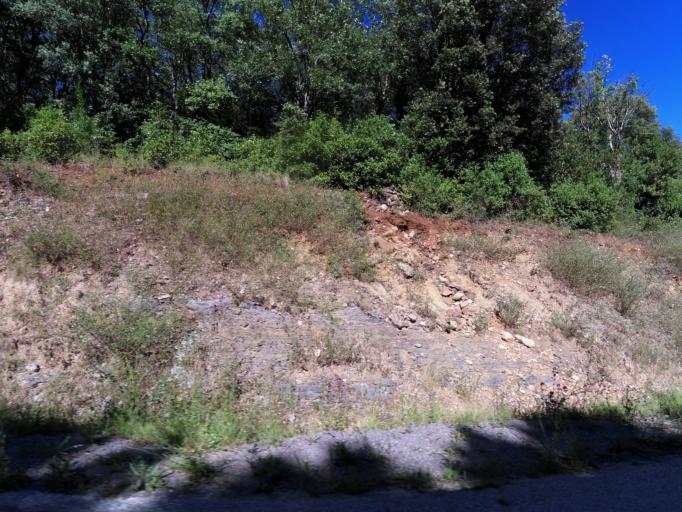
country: FR
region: Languedoc-Roussillon
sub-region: Departement du Gard
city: Saint-Jean-du-Gard
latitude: 44.0858
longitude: 3.9192
